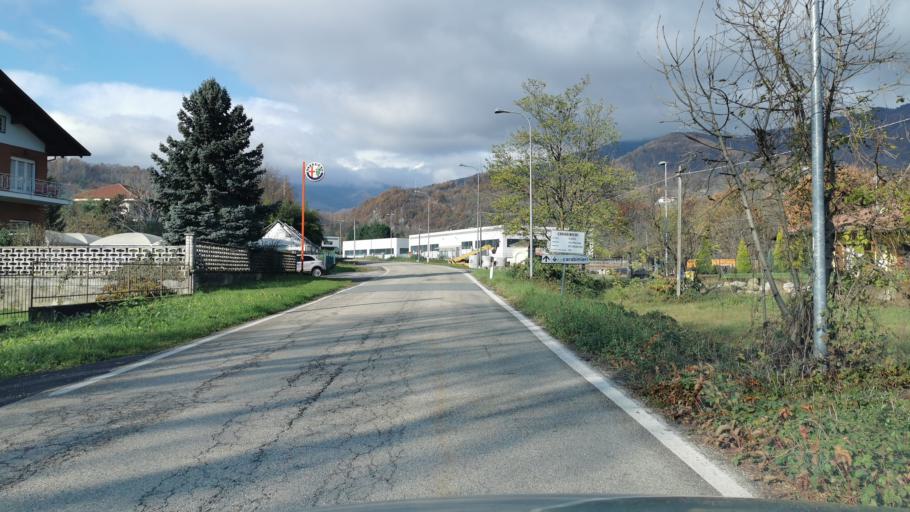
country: IT
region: Piedmont
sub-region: Provincia di Torino
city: Rocca Canavese
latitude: 45.3061
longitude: 7.5818
